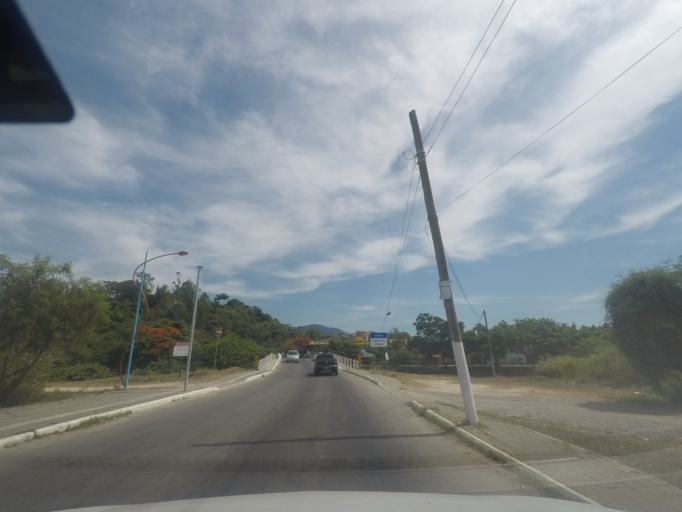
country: BR
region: Rio de Janeiro
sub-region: Marica
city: Marica
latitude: -22.9453
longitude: -42.7518
